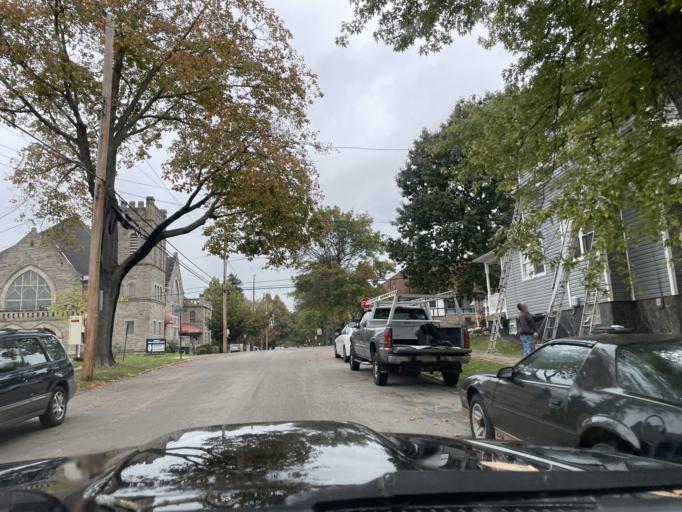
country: US
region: Pennsylvania
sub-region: Allegheny County
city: Oakmont
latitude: 40.5184
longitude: -79.8393
